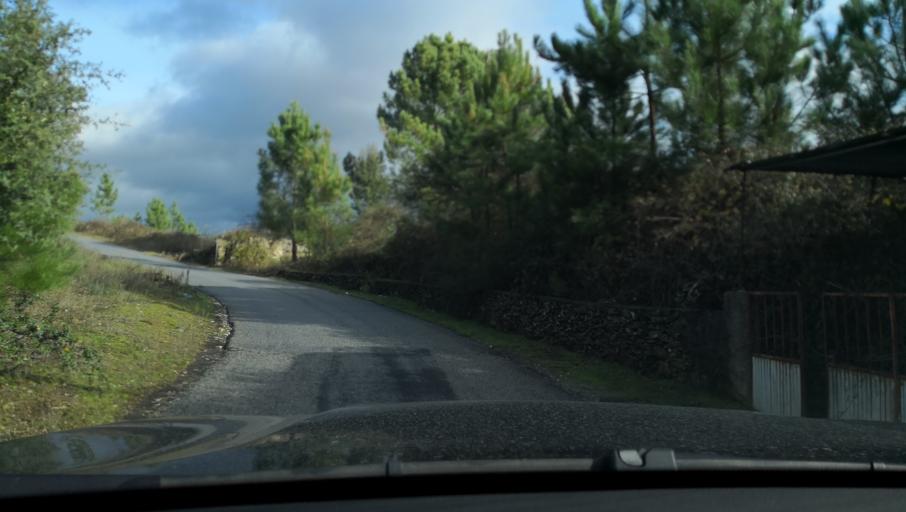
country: PT
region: Vila Real
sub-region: Vila Real
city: Vila Real
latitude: 41.2695
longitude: -7.7157
